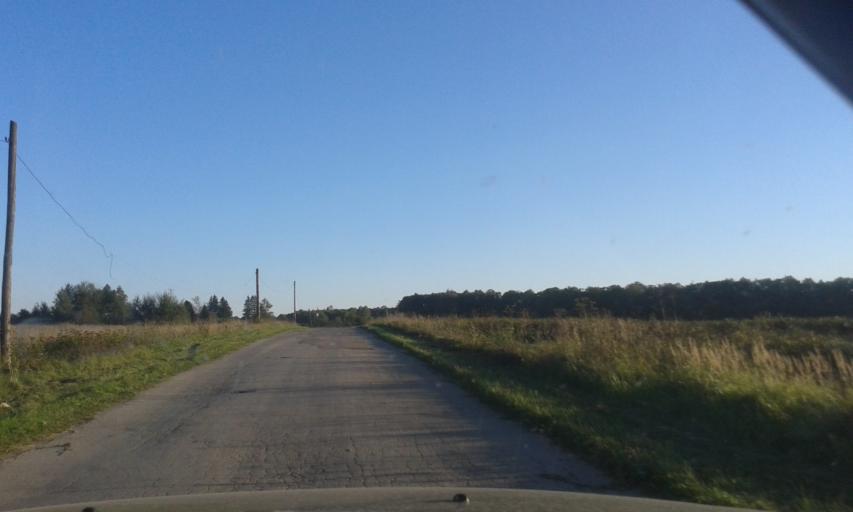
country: RU
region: Tula
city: Krapivna
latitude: 54.1184
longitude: 37.1525
